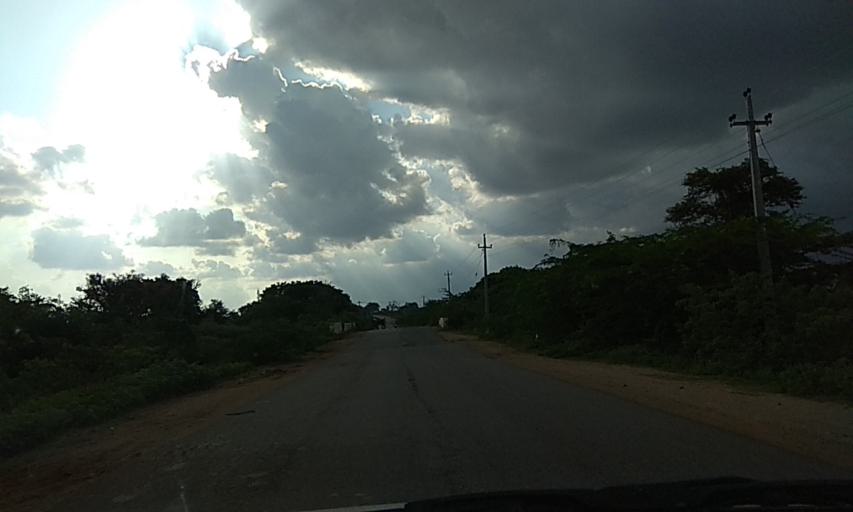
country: IN
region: Karnataka
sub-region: Chamrajnagar
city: Gundlupet
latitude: 11.8141
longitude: 76.7638
